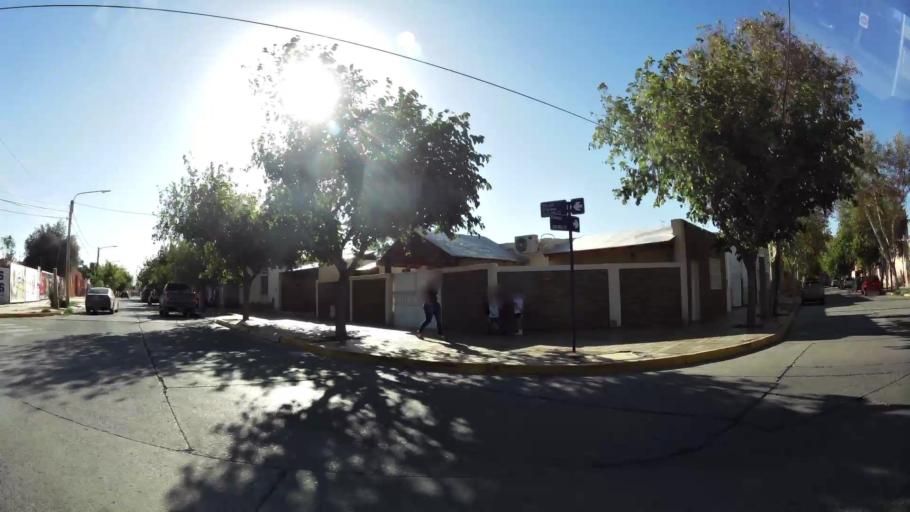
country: AR
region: San Juan
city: San Juan
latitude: -31.5445
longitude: -68.5164
